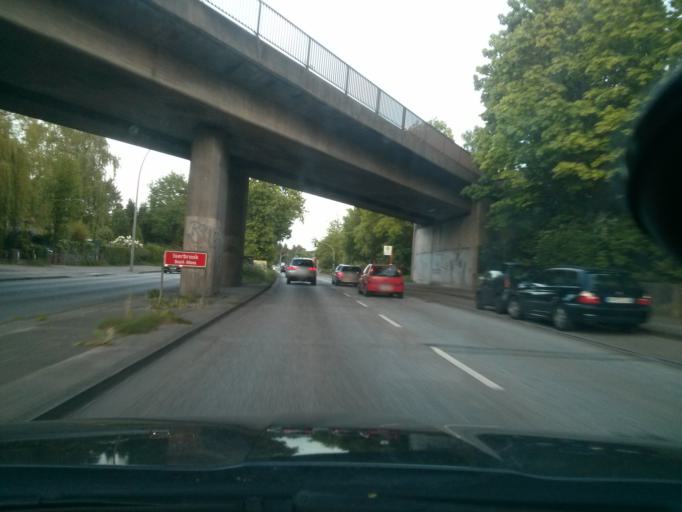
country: DE
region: Schleswig-Holstein
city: Halstenbek
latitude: 53.5777
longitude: 9.8114
